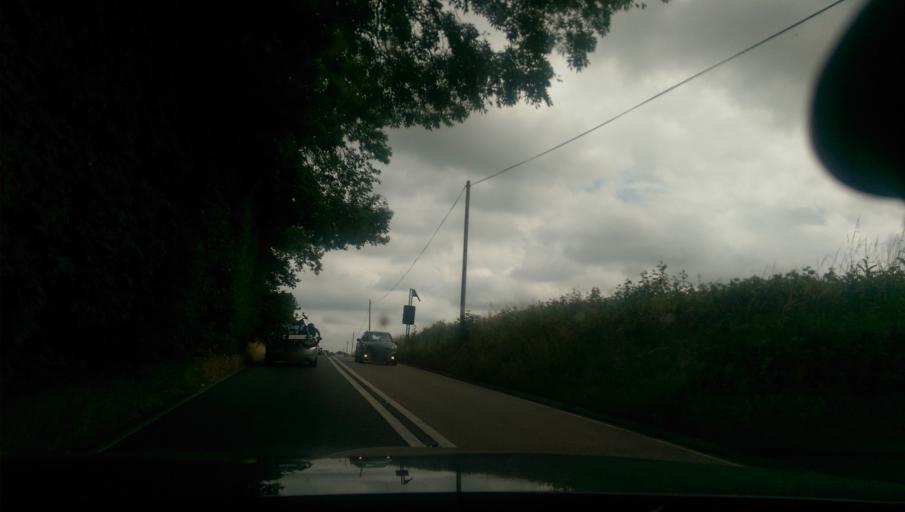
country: GB
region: England
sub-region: Devon
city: Honiton
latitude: 50.8510
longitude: -3.1255
